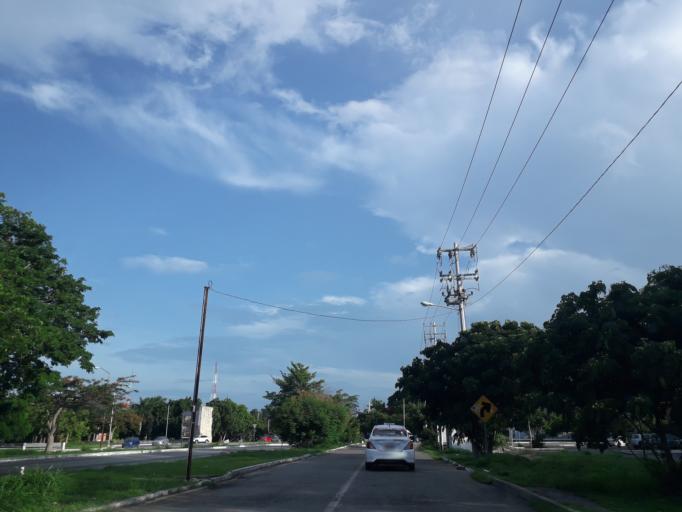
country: MX
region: Yucatan
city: Merida
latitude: 21.0288
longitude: -89.6270
